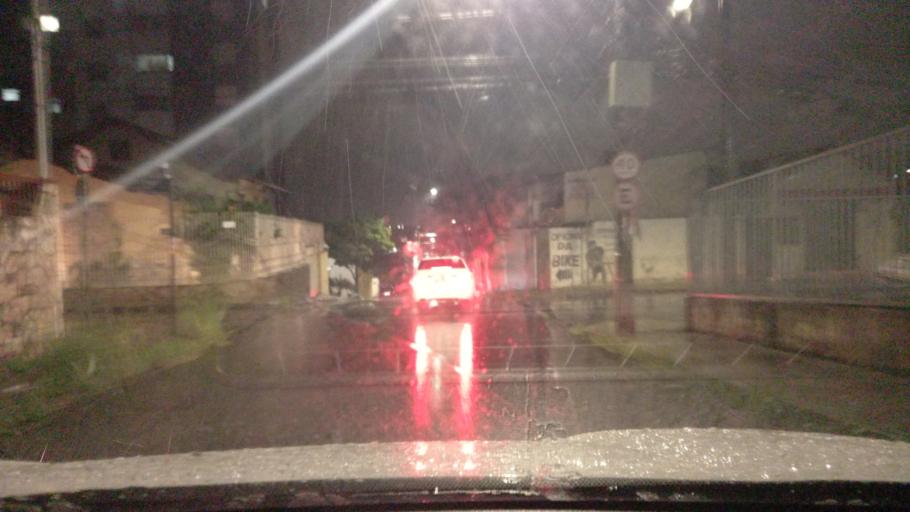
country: BR
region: Minas Gerais
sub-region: Belo Horizonte
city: Belo Horizonte
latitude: -19.9052
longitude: -43.9731
